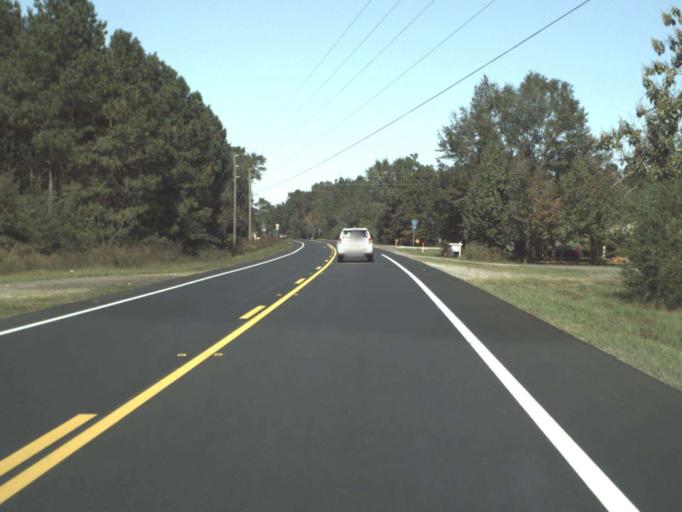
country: US
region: Alabama
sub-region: Covington County
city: Florala
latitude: 30.9436
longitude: -86.2834
